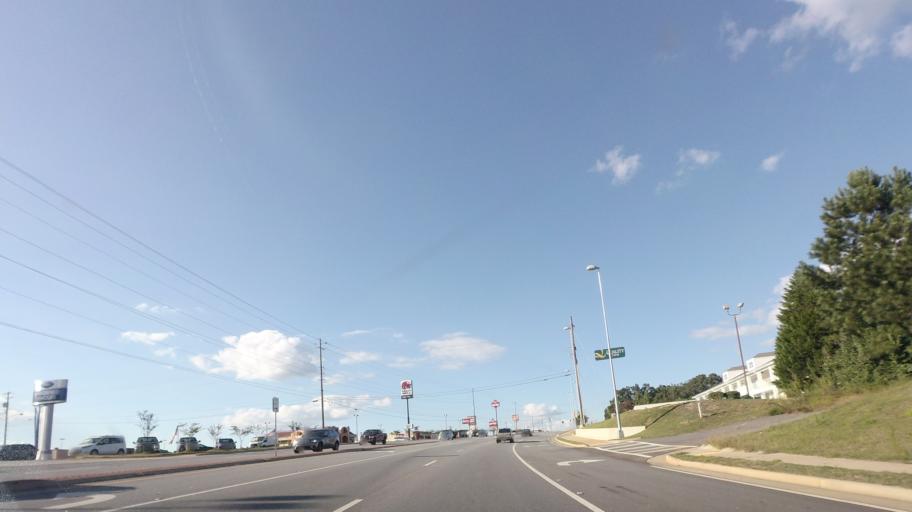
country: US
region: Georgia
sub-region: Upson County
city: Hannahs Mill
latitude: 32.9195
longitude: -84.3340
